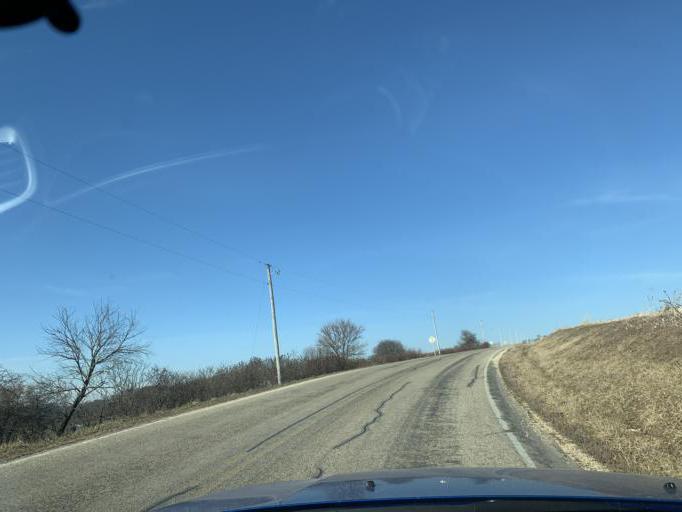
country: US
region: Wisconsin
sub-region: Iowa County
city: Barneveld
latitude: 42.8510
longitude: -89.9357
